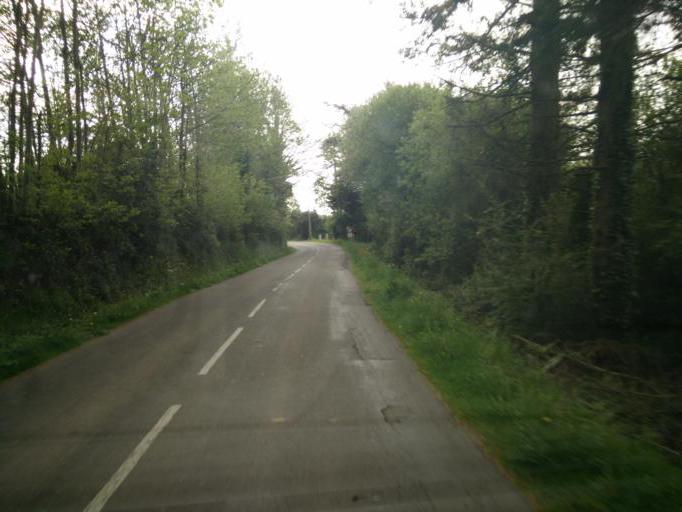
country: FR
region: Brittany
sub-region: Departement du Finistere
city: Tremeven
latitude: 47.9097
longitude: -3.5172
